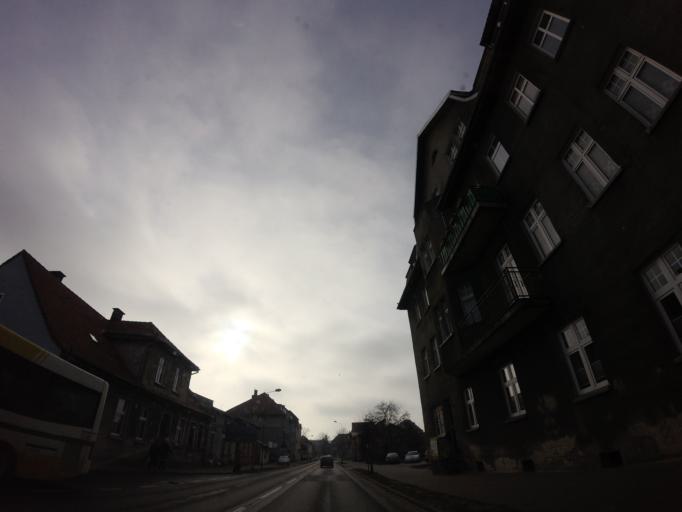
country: PL
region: West Pomeranian Voivodeship
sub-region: Powiat walecki
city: Walcz
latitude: 53.2761
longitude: 16.4640
